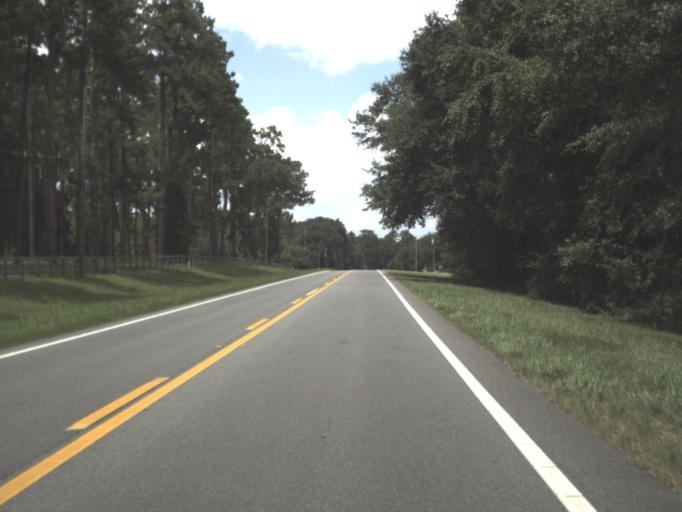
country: US
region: Florida
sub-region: Madison County
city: Madison
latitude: 30.4996
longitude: -83.3816
